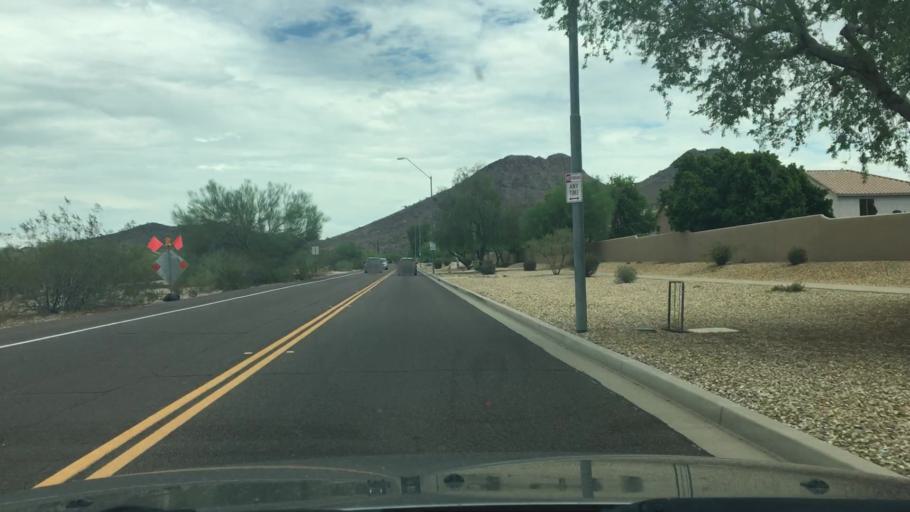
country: US
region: Arizona
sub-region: Maricopa County
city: Sun City
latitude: 33.7250
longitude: -112.2076
